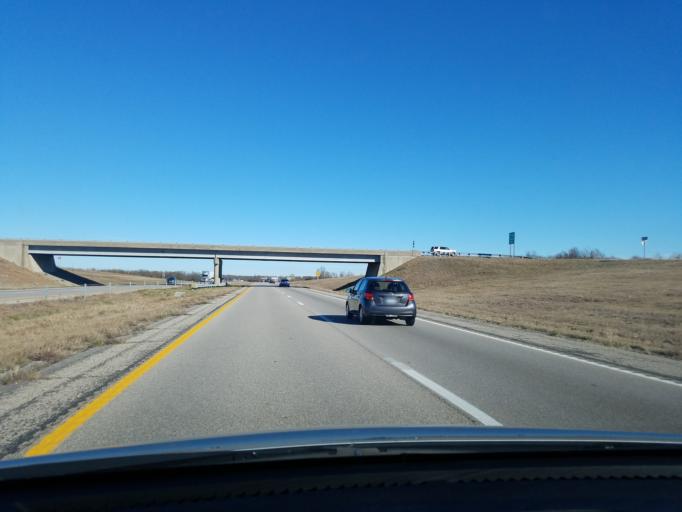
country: US
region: Missouri
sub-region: Laclede County
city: Lebanon
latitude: 37.5991
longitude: -92.7162
